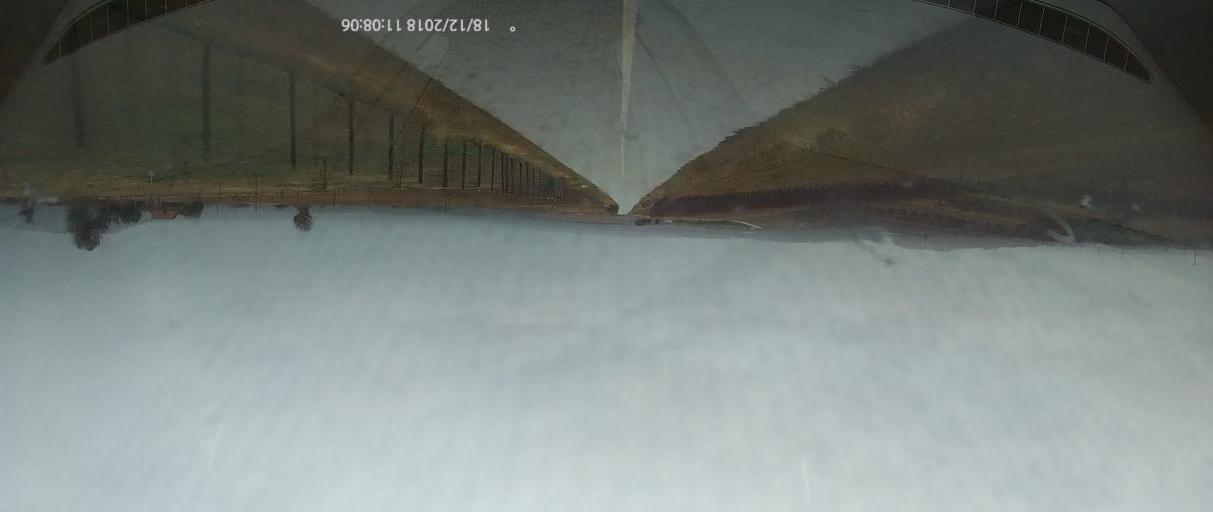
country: GR
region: Central Macedonia
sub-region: Nomos Pierias
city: Kato Milia
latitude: 40.2259
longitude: 22.3429
